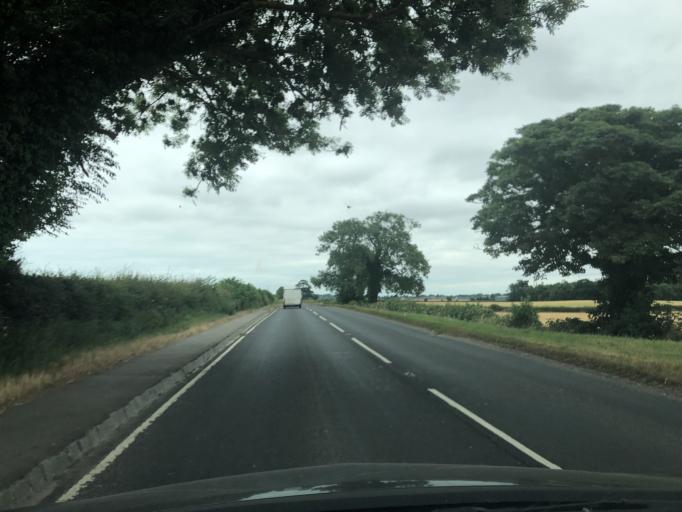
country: GB
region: England
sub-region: North Yorkshire
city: East Ayton
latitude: 54.2502
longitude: -0.4702
